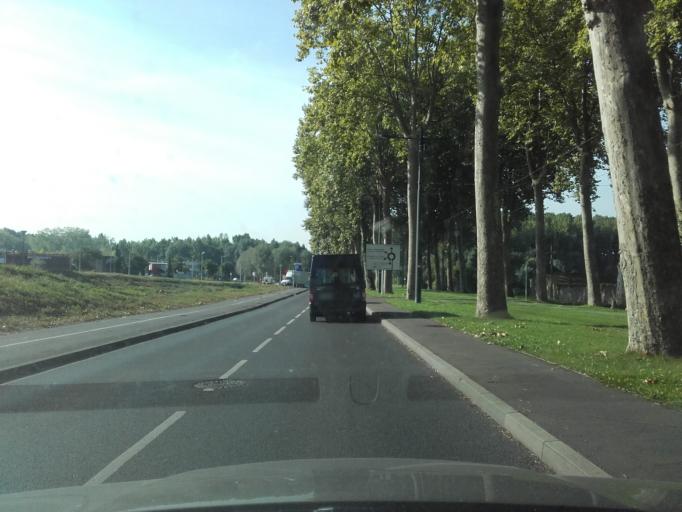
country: FR
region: Centre
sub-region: Departement d'Indre-et-Loire
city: Joue-les-Tours
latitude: 47.3670
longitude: 0.6757
